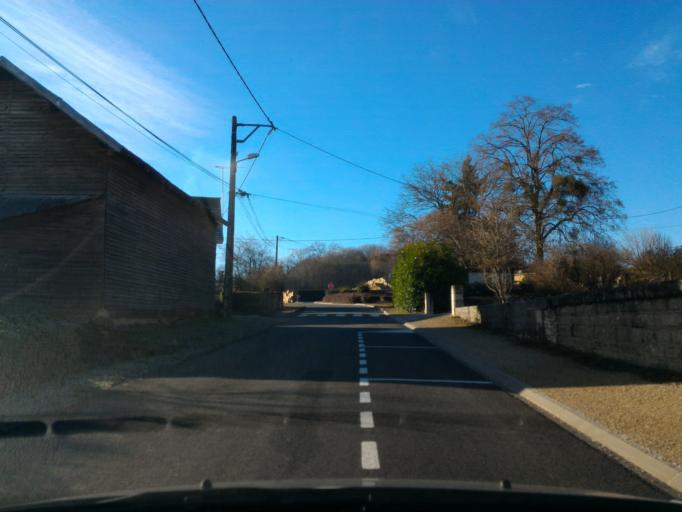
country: FR
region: Poitou-Charentes
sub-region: Departement de la Charente
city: Champagne-Mouton
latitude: 45.9875
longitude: 0.4045
